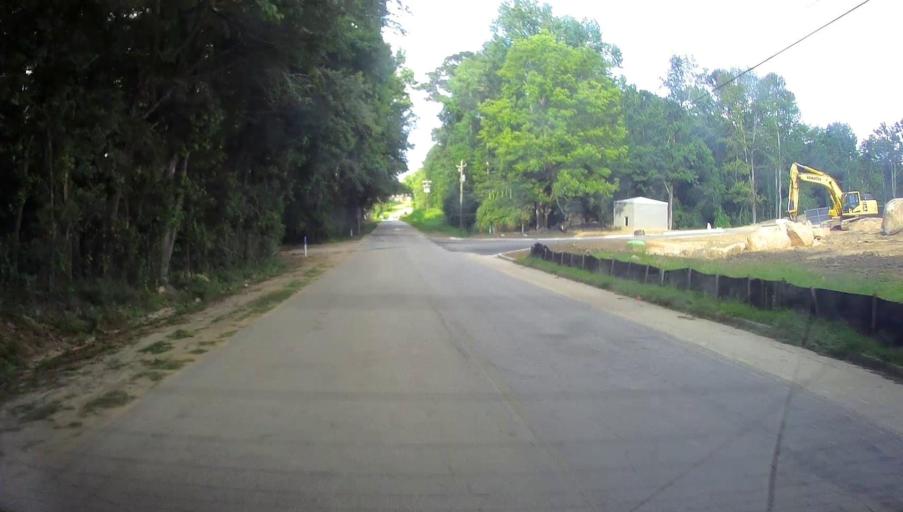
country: US
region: Georgia
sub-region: Crawford County
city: Knoxville
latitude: 32.7223
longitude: -84.0049
